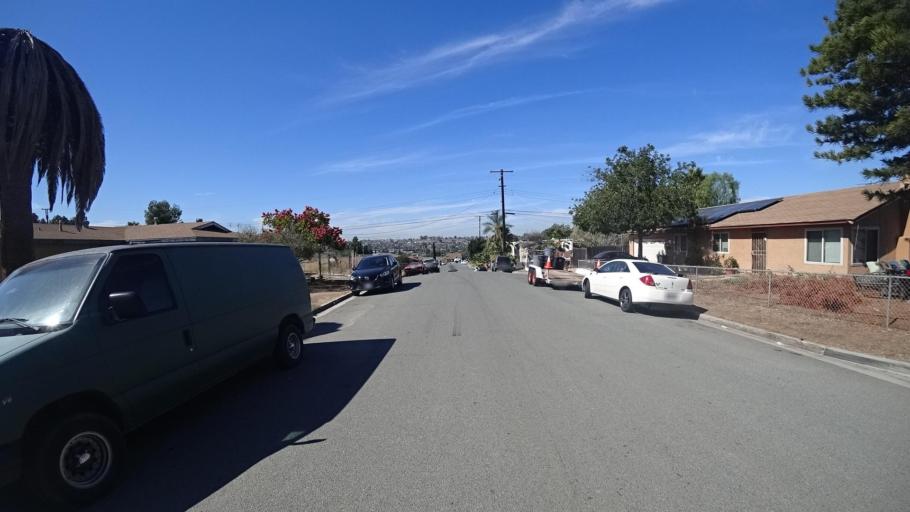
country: US
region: California
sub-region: San Diego County
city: La Presa
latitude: 32.7061
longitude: -116.9990
